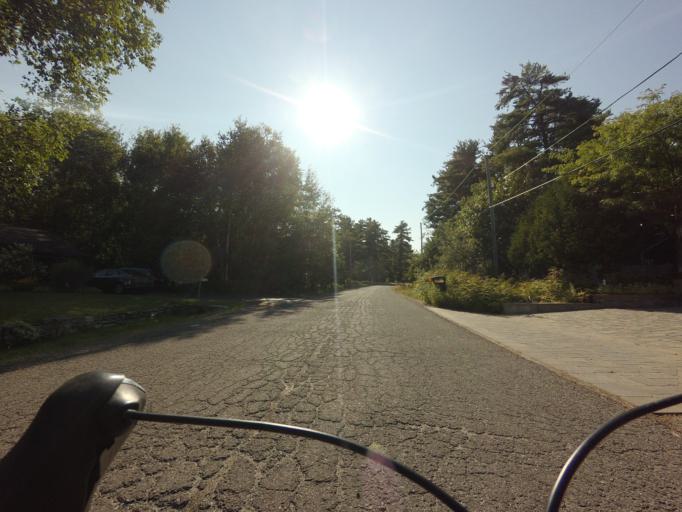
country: CA
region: Ontario
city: Bells Corners
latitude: 45.4868
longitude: -76.0405
